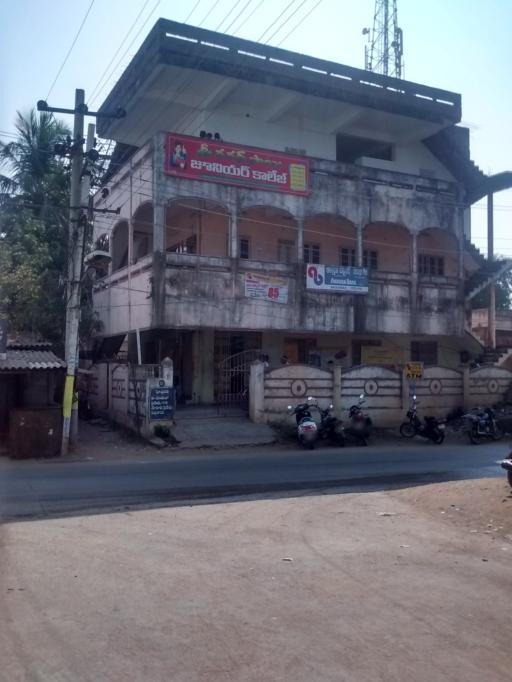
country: IN
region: Andhra Pradesh
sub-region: West Godavari
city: Akividu
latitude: 16.5377
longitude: 81.4088
